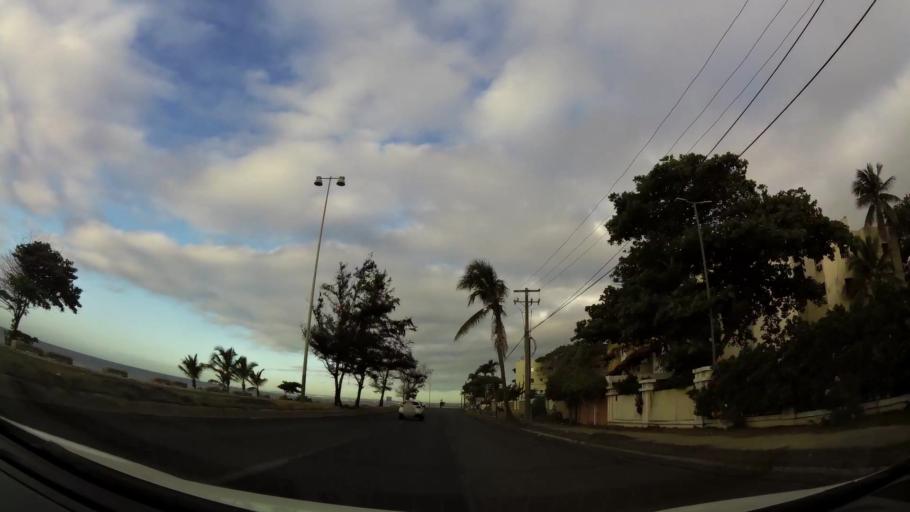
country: DO
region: Nacional
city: Bella Vista
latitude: 18.4277
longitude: -69.9694
